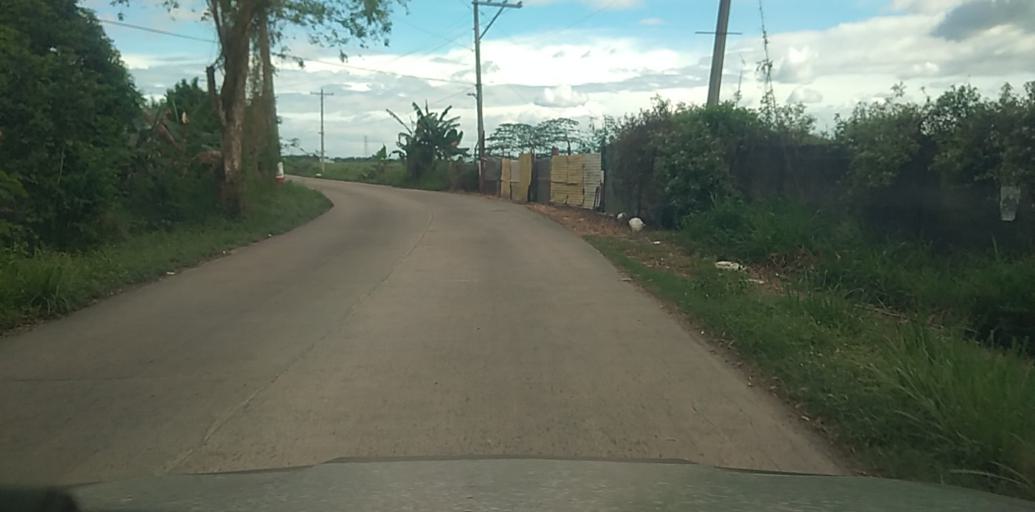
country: PH
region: Central Luzon
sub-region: Province of Pampanga
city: Pandacaqui
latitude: 15.1758
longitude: 120.6675
